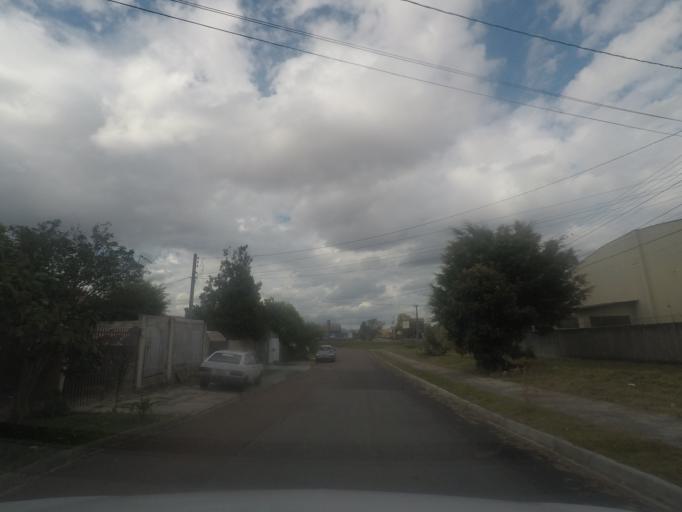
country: BR
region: Parana
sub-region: Pinhais
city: Pinhais
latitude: -25.4628
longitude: -49.2194
